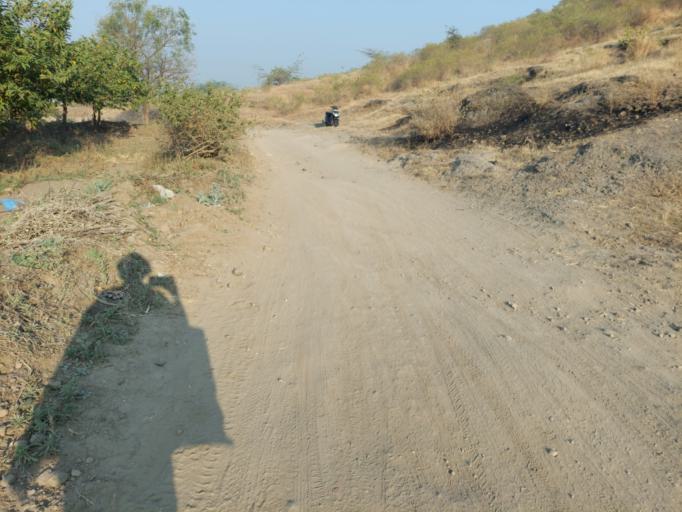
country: IN
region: Maharashtra
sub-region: Pune Division
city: Sasvad
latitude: 18.4223
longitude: 73.9967
